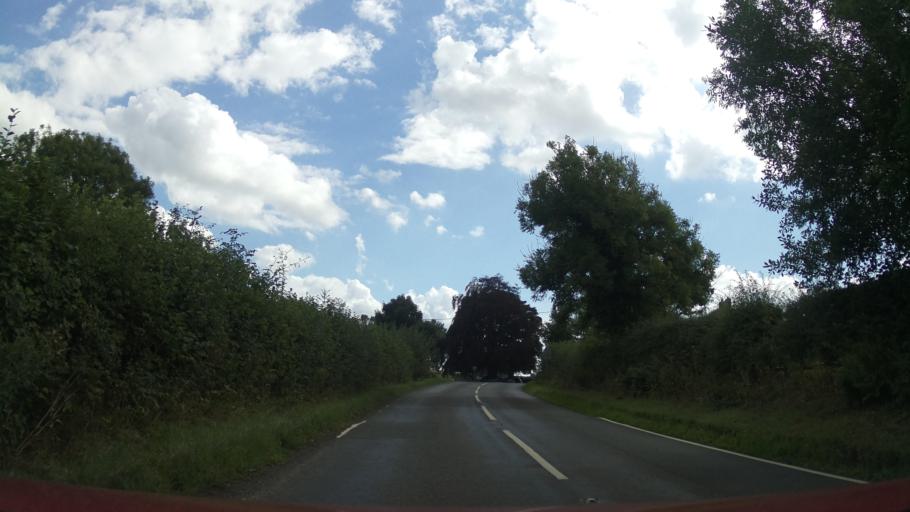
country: GB
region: England
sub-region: North Yorkshire
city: Leyburn
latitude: 54.3772
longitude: -1.8300
